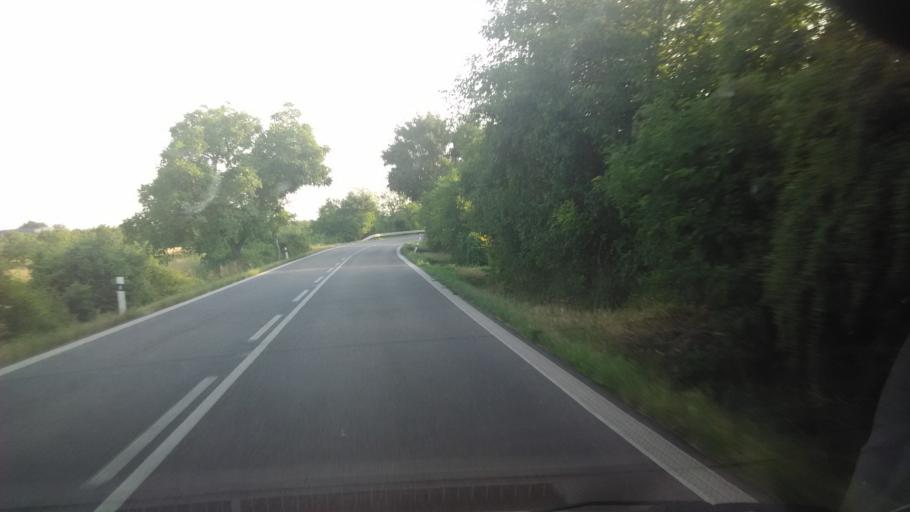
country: SK
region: Nitriansky
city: Tlmace
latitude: 48.2796
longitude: 18.5207
